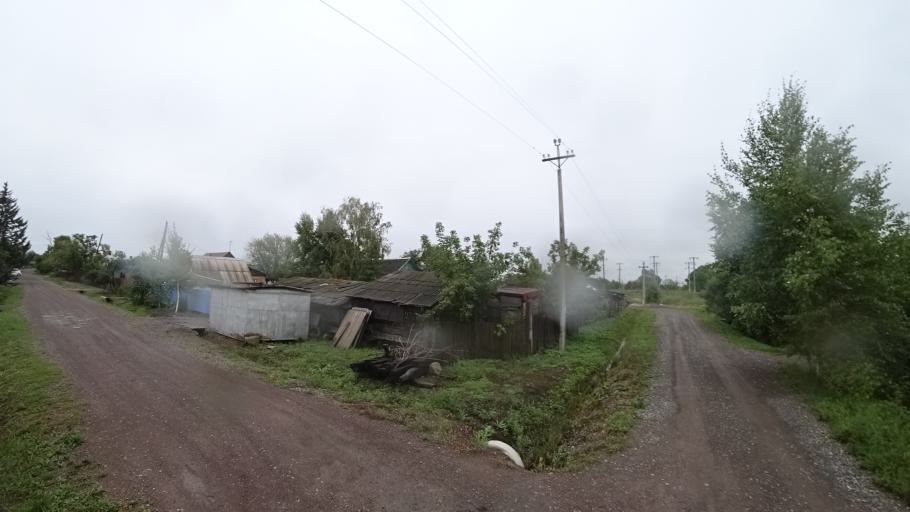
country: RU
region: Primorskiy
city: Monastyrishche
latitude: 44.1904
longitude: 132.4209
